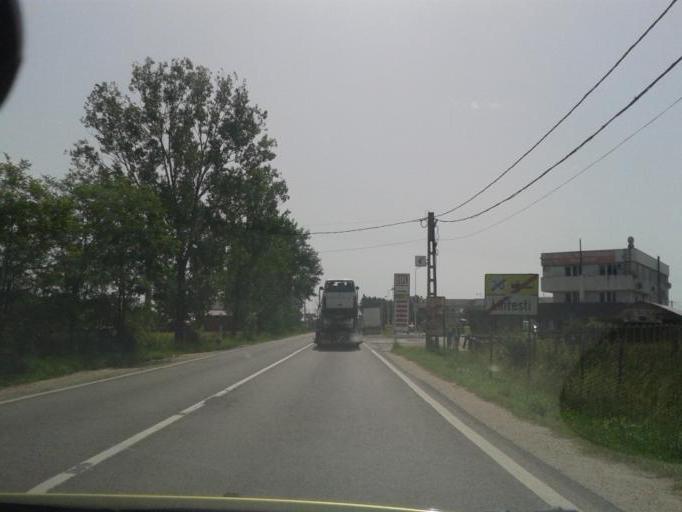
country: RO
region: Arges
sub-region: Comuna Cotmeana
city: Cotmeana
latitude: 44.9988
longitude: 24.6165
